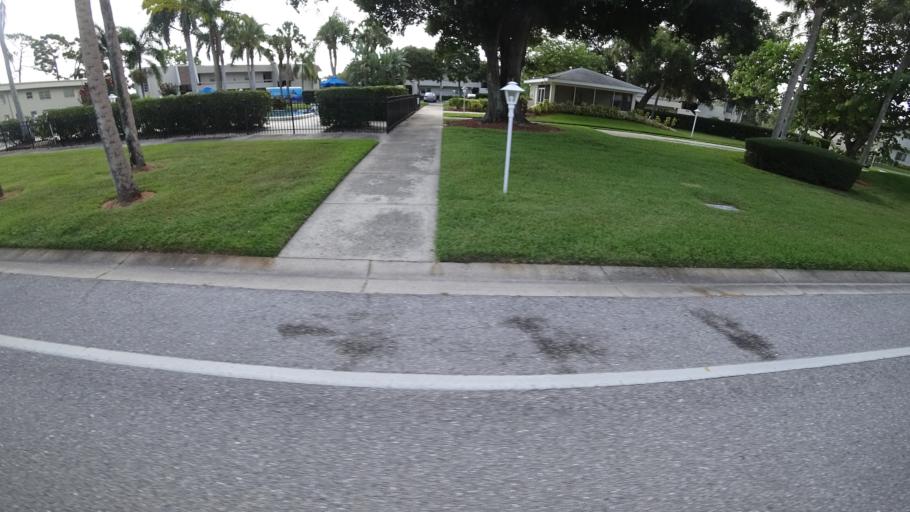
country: US
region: Florida
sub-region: Sarasota County
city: Desoto Lakes
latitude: 27.4123
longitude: -82.4970
